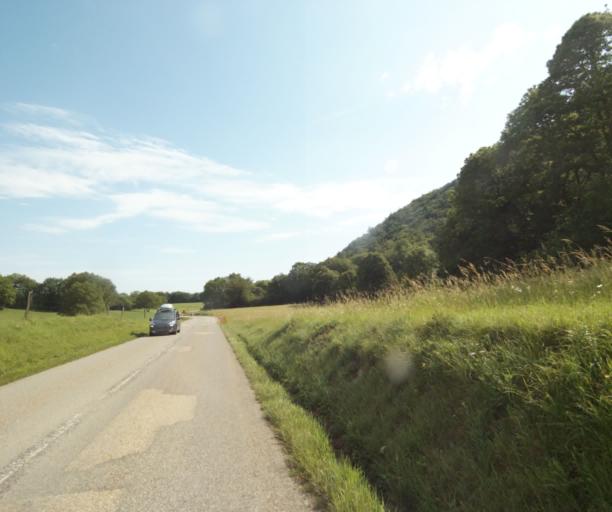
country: FR
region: Rhone-Alpes
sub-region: Departement de la Haute-Savoie
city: Lyaud
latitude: 46.3303
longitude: 6.5095
